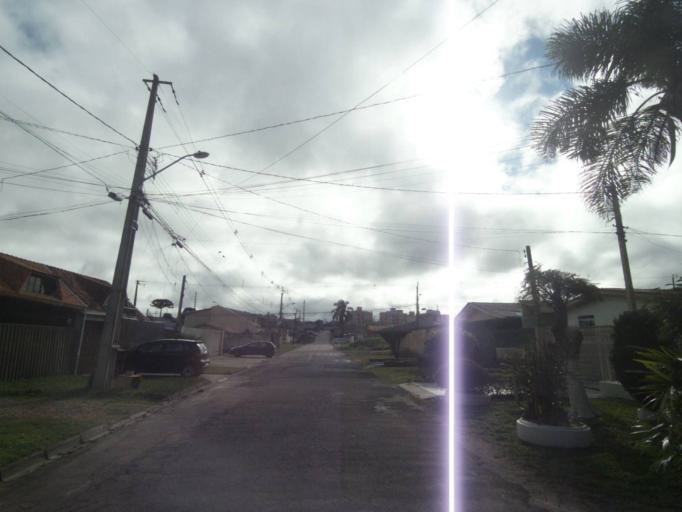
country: BR
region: Parana
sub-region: Sao Jose Dos Pinhais
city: Sao Jose dos Pinhais
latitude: -25.5244
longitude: -49.3031
